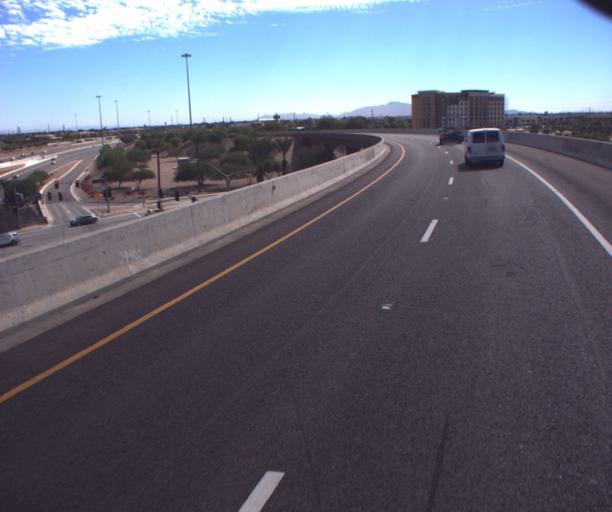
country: US
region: Arizona
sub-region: Maricopa County
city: Chandler
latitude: 33.2917
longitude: -111.8934
